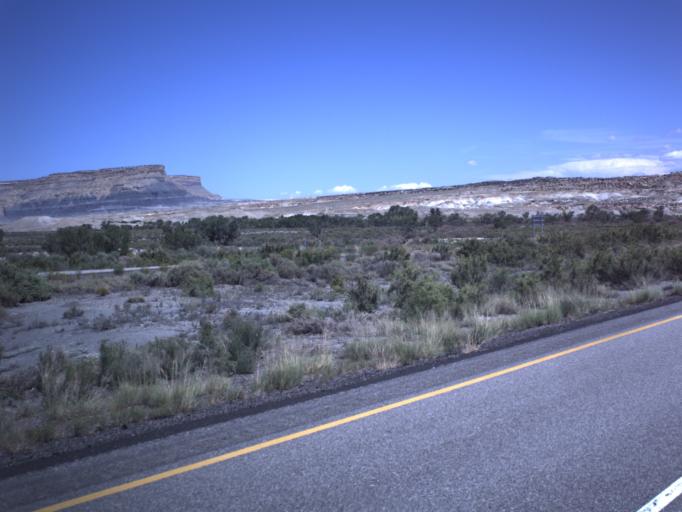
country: US
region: Utah
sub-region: Emery County
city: Ferron
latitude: 38.8113
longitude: -111.2077
